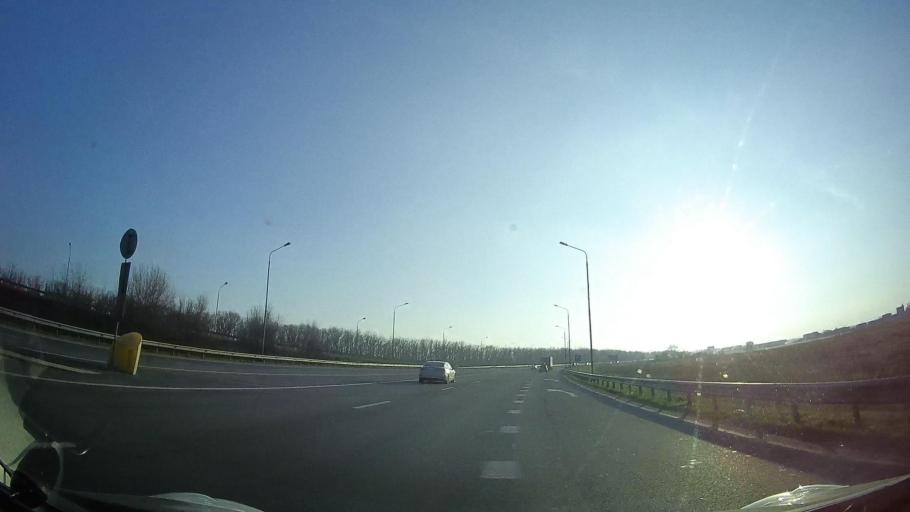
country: RU
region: Rostov
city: Ol'ginskaya
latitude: 47.1284
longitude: 39.8752
